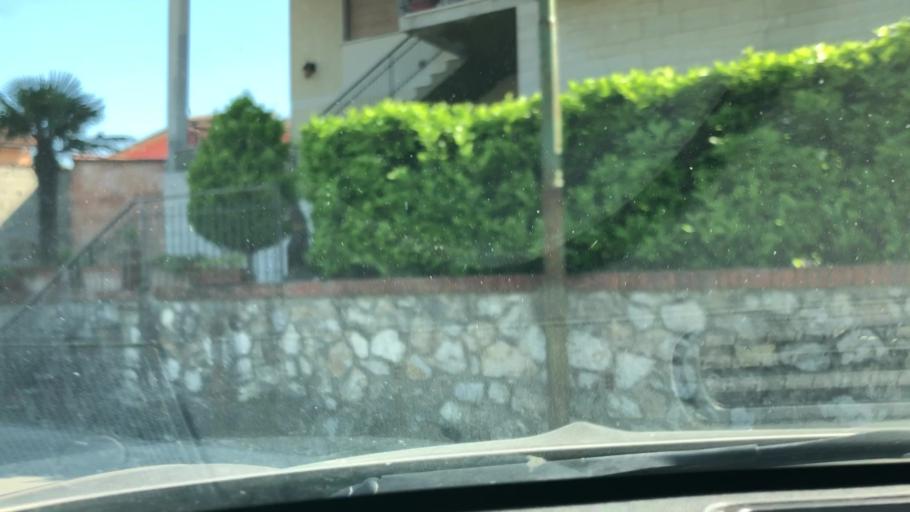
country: IT
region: Tuscany
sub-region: Province of Pisa
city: Capannoli
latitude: 43.5881
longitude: 10.6755
